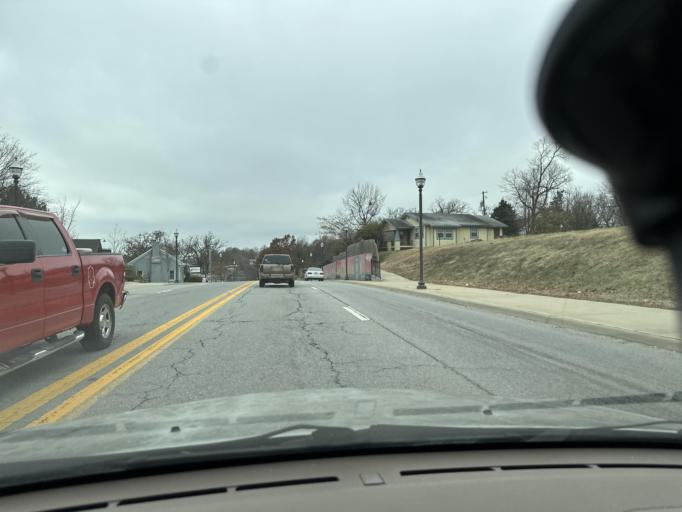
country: US
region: Arkansas
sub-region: Washington County
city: Fayetteville
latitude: 36.0750
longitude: -94.1572
